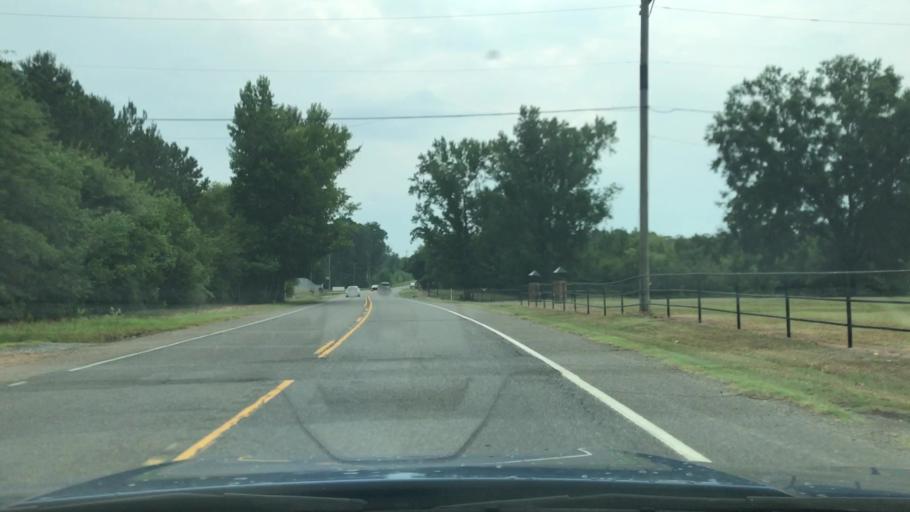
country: US
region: Texas
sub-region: Harrison County
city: Waskom
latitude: 32.4654
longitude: -94.0346
